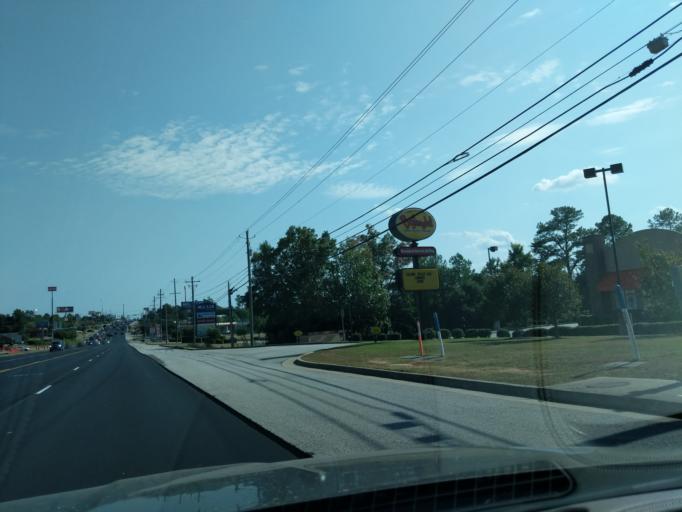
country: US
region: Georgia
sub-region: Columbia County
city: Evans
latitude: 33.4889
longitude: -82.1353
